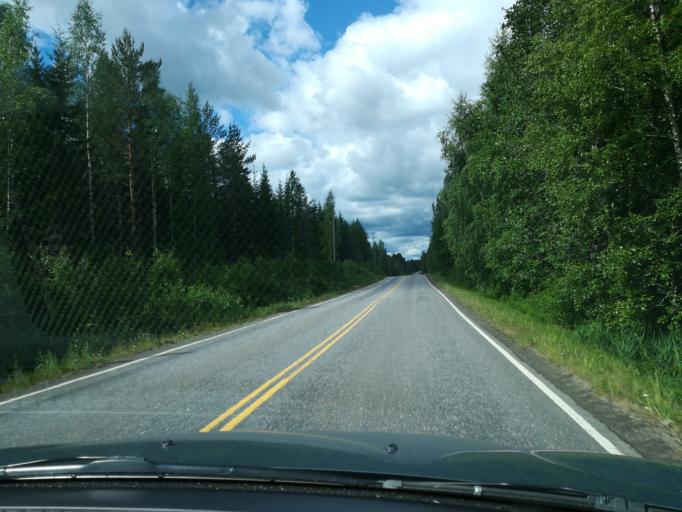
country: FI
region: Southern Savonia
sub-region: Mikkeli
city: Maentyharju
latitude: 61.3628
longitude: 27.0519
